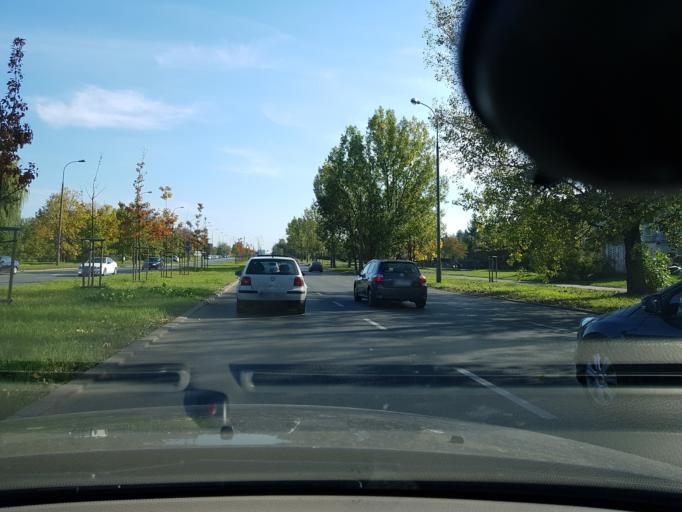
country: PL
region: Masovian Voivodeship
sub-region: Warszawa
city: Ursynow
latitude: 52.1665
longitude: 21.0339
